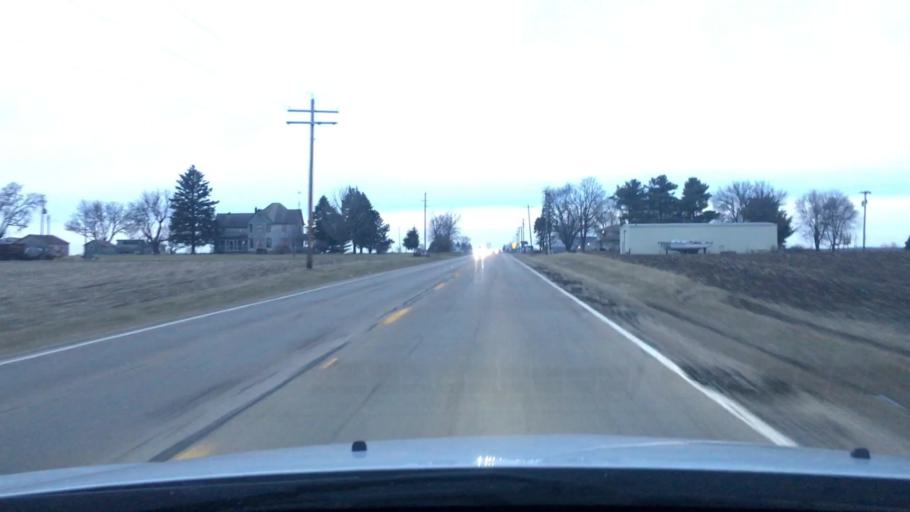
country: US
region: Illinois
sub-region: LaSalle County
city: Peru
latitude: 41.3926
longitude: -89.1258
